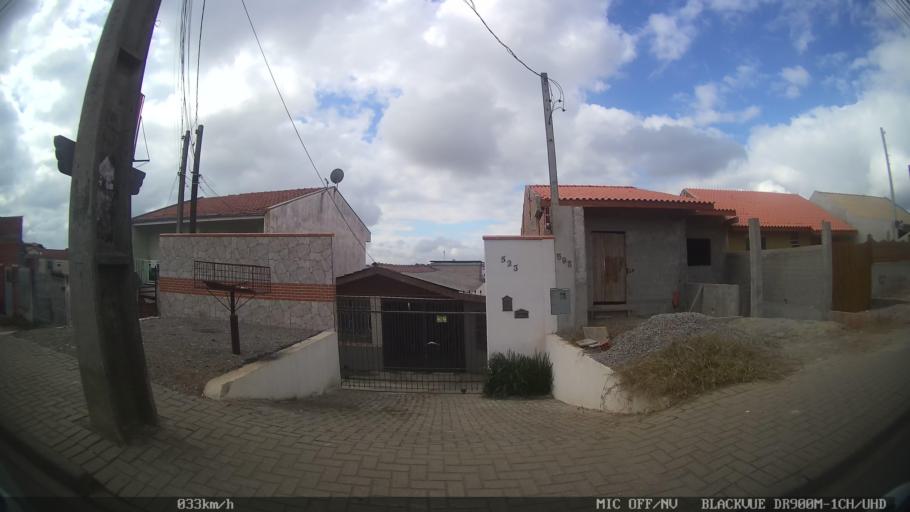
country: BR
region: Parana
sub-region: Colombo
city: Colombo
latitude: -25.3645
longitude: -49.2015
